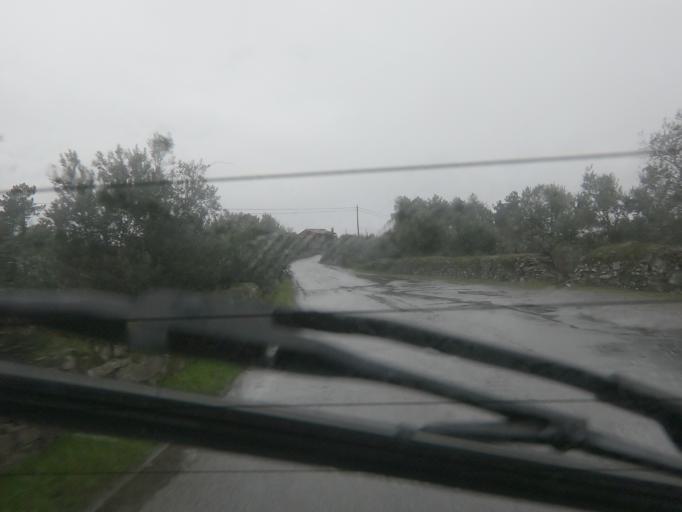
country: PT
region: Vila Real
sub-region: Peso da Regua
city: Peso da Regua
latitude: 41.1916
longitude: -7.7089
